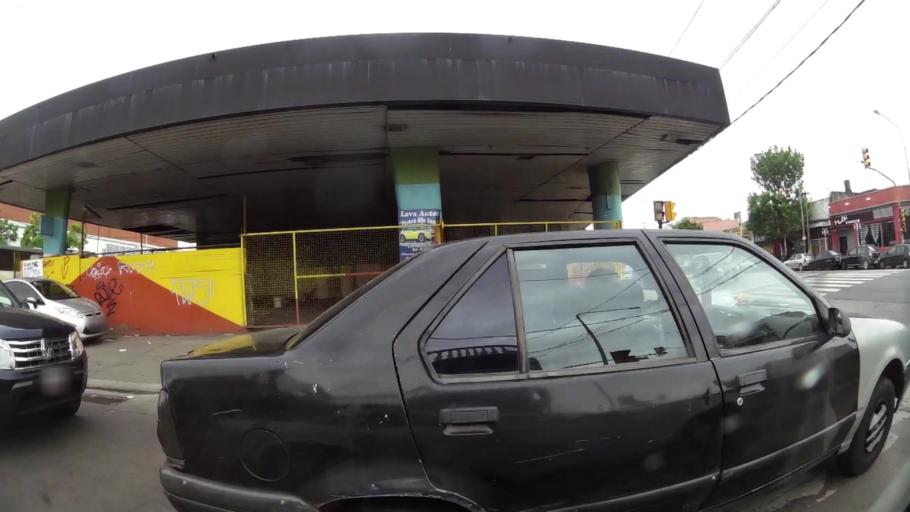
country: AR
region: Buenos Aires
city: San Justo
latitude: -34.6661
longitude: -58.5274
